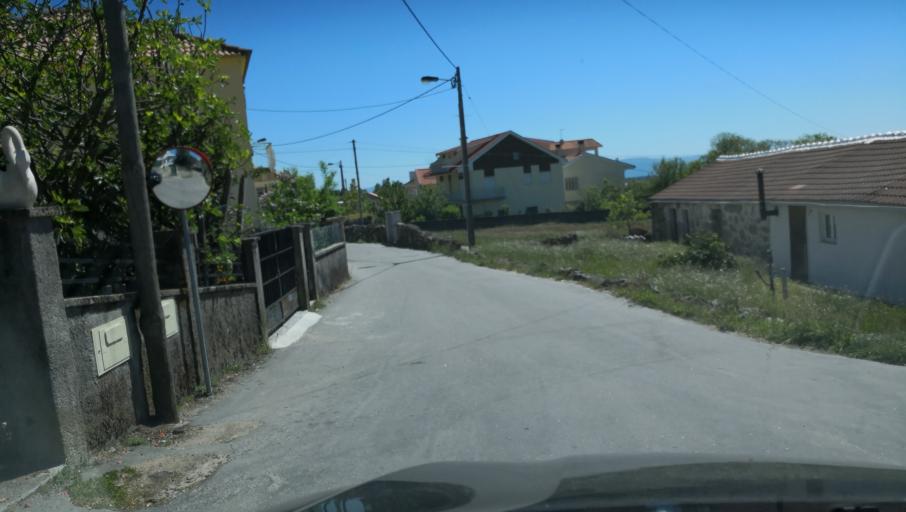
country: PT
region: Vila Real
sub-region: Vila Real
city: Vila Real
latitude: 41.2990
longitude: -7.6592
